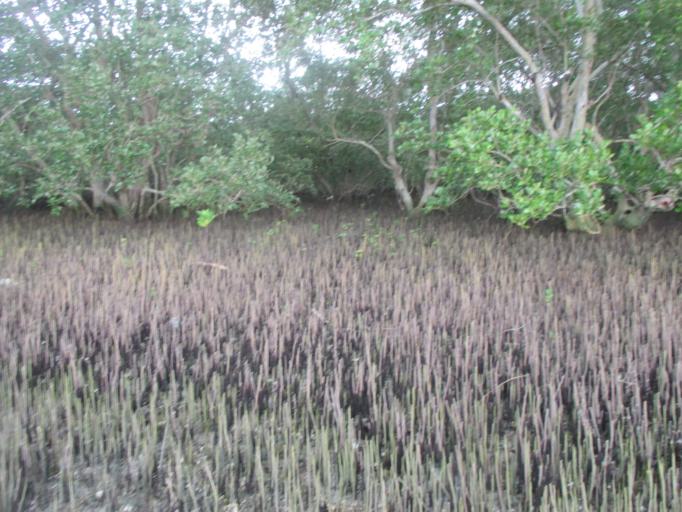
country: PH
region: Calabarzon
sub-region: Province of Batangas
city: Binubusan
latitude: 13.9687
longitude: 120.6231
